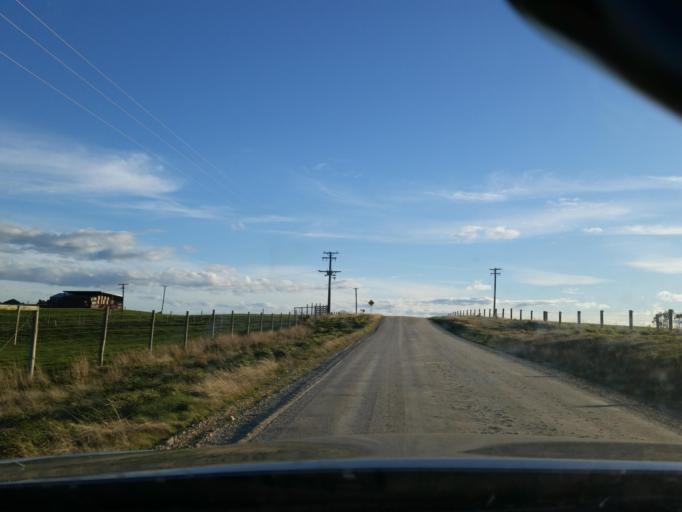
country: NZ
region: Southland
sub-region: Gore District
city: Gore
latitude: -46.3579
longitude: 168.7213
